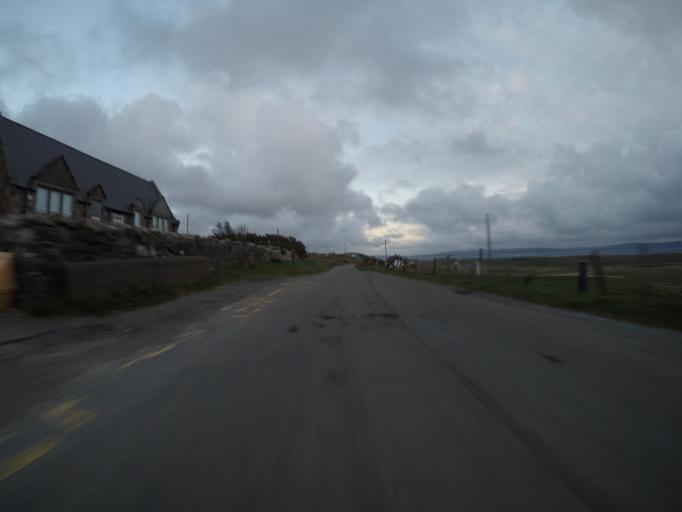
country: GB
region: Scotland
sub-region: Highland
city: Portree
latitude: 57.6357
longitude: -6.3764
